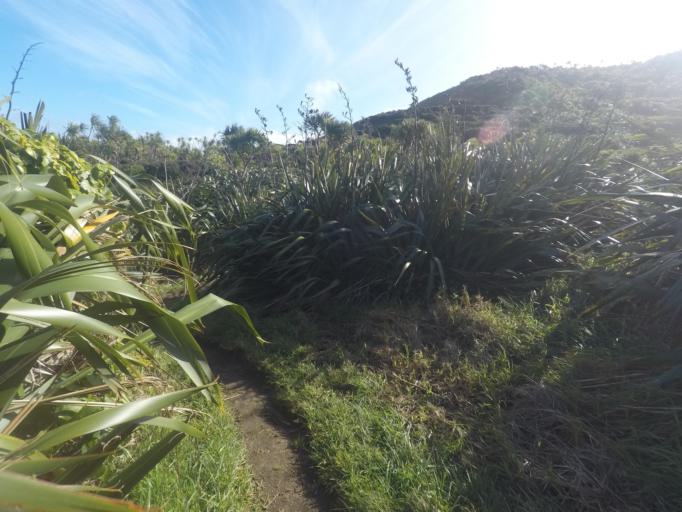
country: NZ
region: Auckland
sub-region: Auckland
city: Muriwai Beach
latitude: -36.8602
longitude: 174.4342
